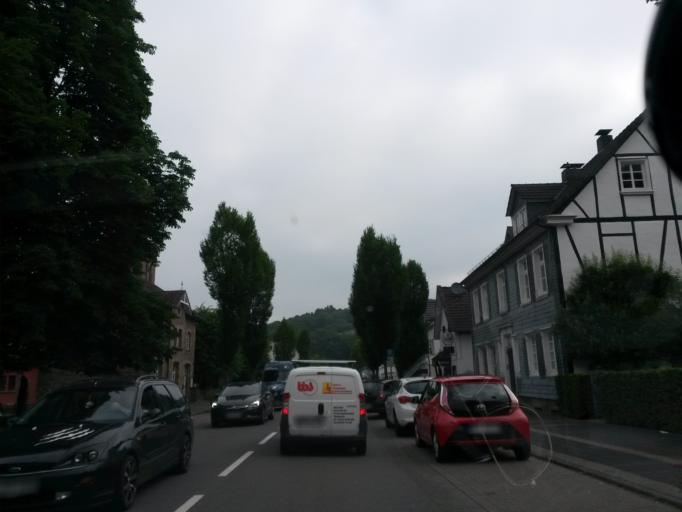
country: DE
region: North Rhine-Westphalia
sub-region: Regierungsbezirk Koln
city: Engelskirchen
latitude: 50.9845
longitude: 7.4098
